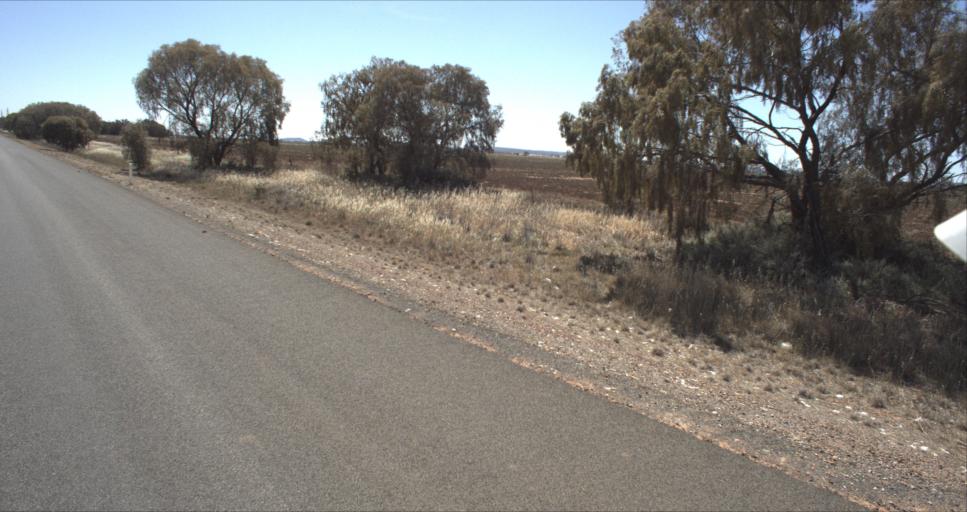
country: AU
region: New South Wales
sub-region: Leeton
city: Leeton
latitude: -34.4772
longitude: 146.2911
